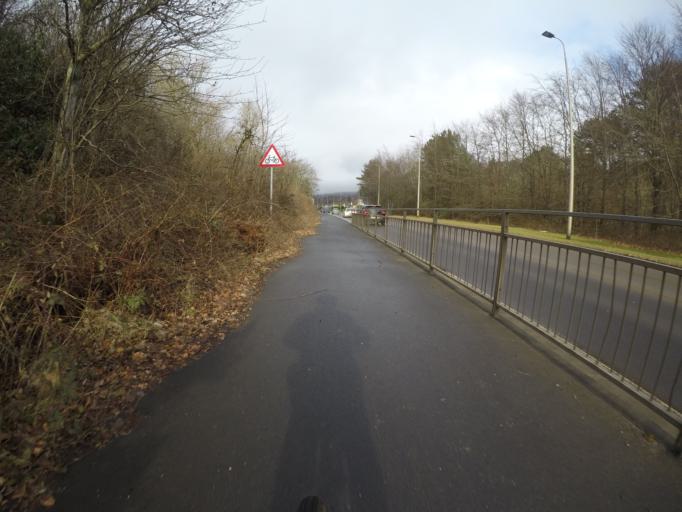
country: GB
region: Scotland
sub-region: North Ayrshire
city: Fairlie
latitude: 55.7456
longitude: -4.8576
